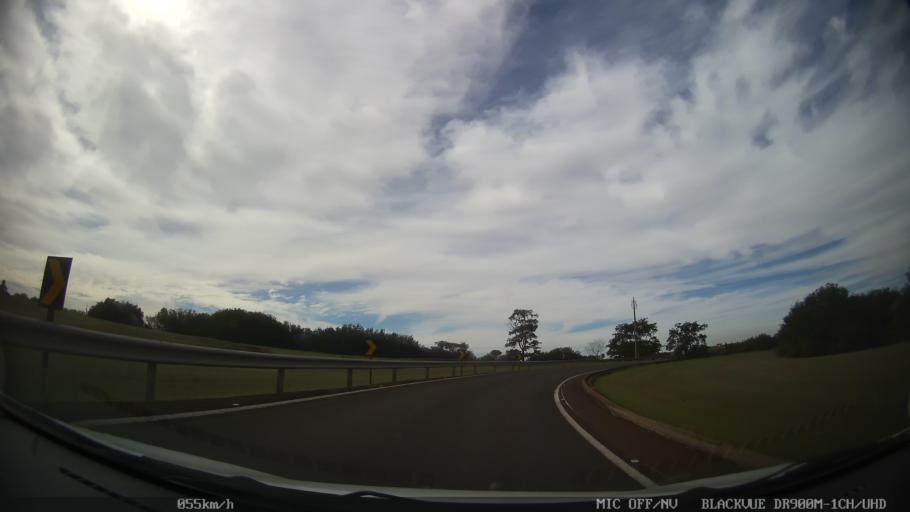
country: BR
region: Sao Paulo
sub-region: Taquaritinga
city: Taquaritinga
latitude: -21.4751
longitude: -48.6003
